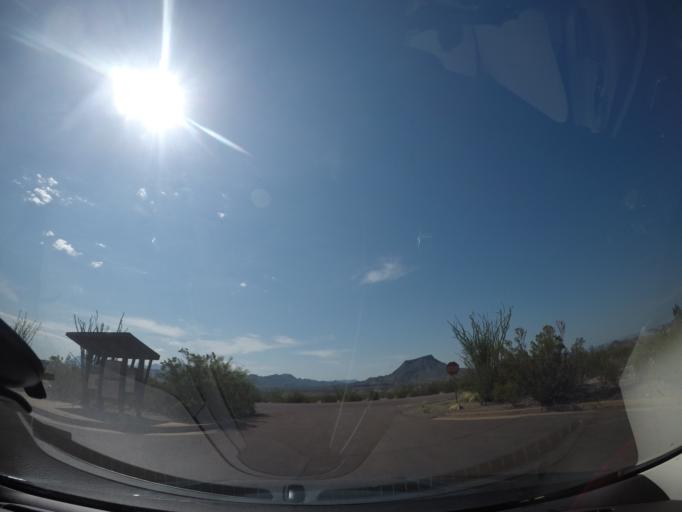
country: US
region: Texas
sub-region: Presidio County
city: Presidio
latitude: 29.2936
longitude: -103.4953
